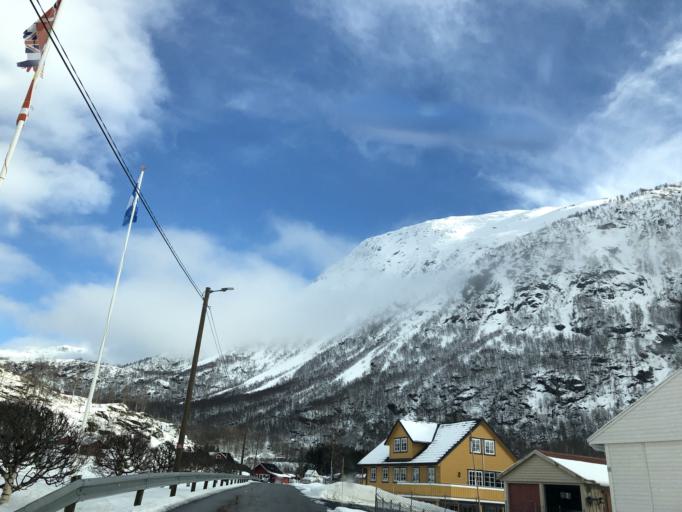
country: NO
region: Hordaland
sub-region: Odda
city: Odda
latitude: 59.8309
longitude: 6.8250
